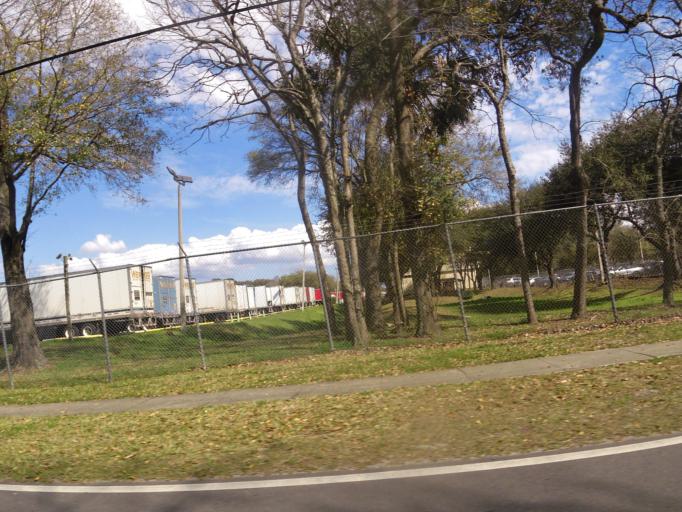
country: US
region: Florida
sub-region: Duval County
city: Jacksonville
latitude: 30.3411
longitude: -81.7141
